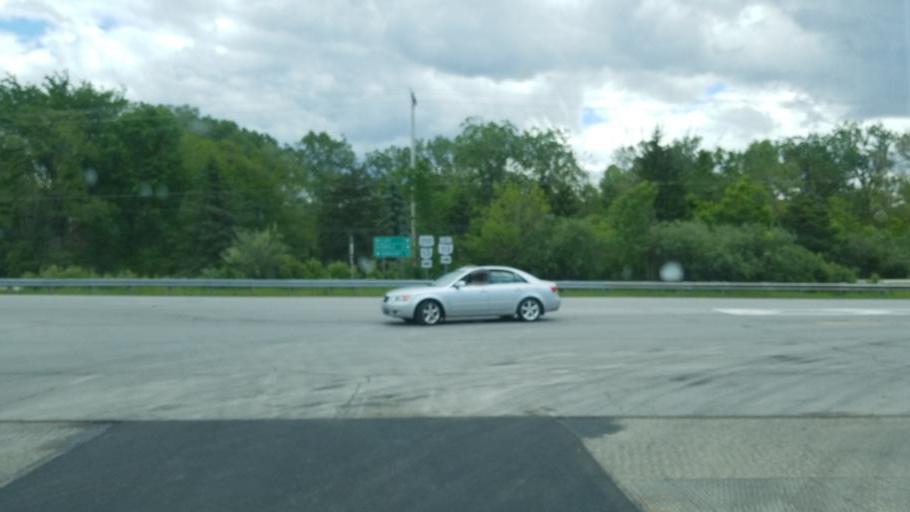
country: US
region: Ohio
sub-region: Erie County
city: Milan
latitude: 41.3038
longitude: -82.6080
